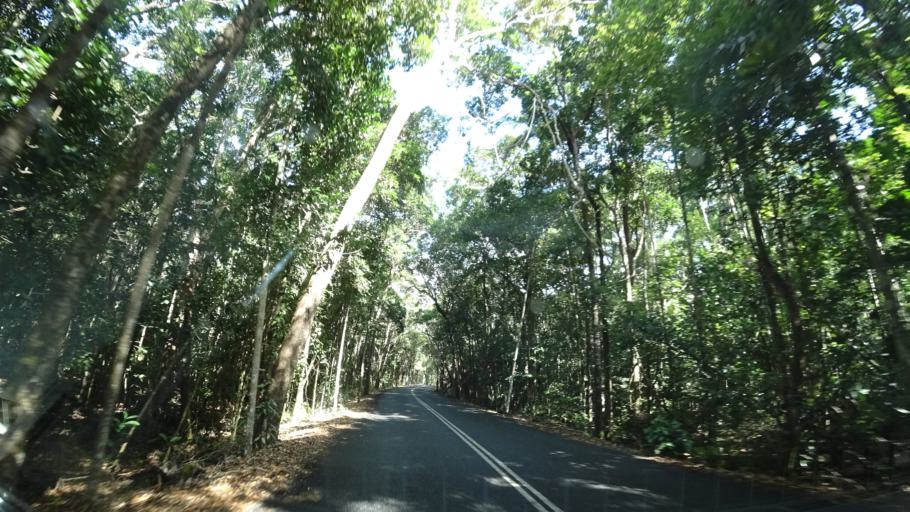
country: AU
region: Queensland
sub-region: Cairns
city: Port Douglas
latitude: -16.1382
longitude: 145.4481
